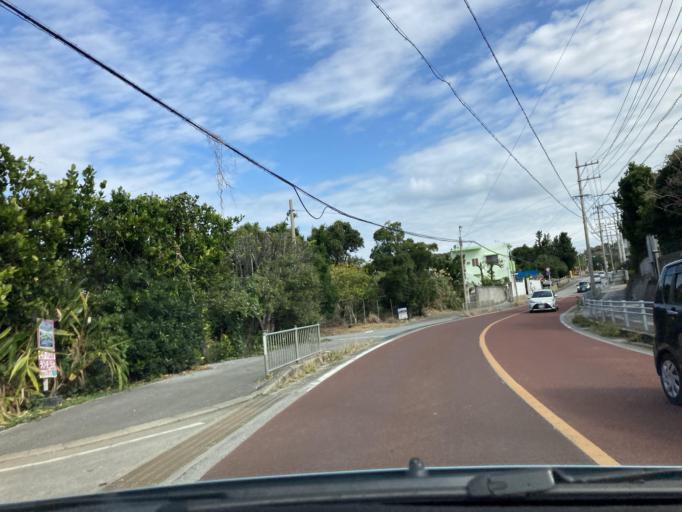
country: JP
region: Okinawa
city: Nago
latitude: 26.6972
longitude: 127.9412
